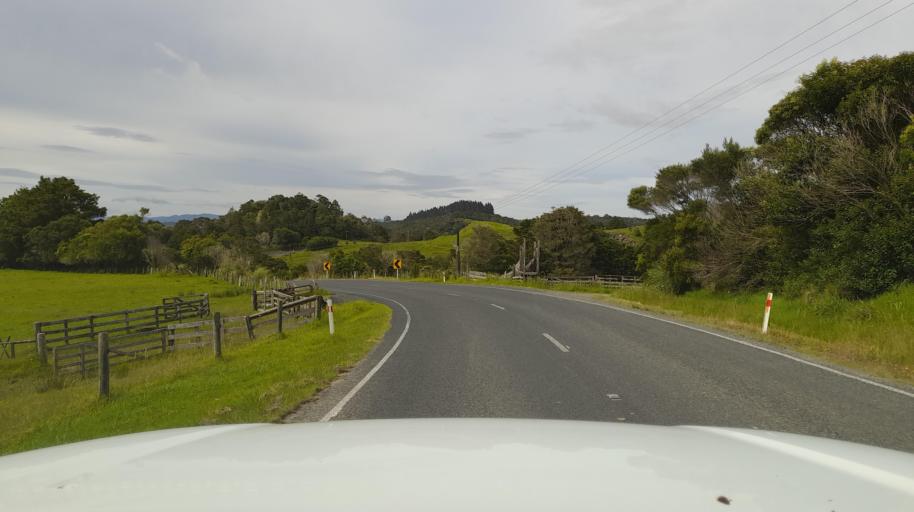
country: NZ
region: Northland
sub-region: Far North District
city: Taipa
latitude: -35.2652
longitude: 173.5248
